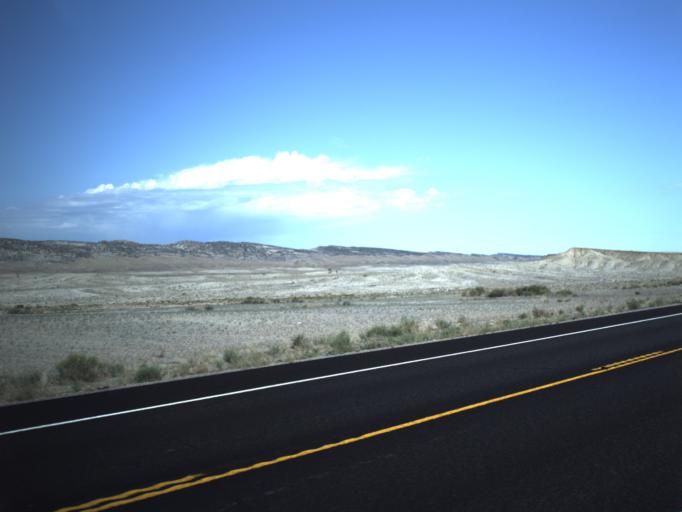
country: US
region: Utah
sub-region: Carbon County
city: East Carbon City
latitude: 39.1458
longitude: -110.3371
